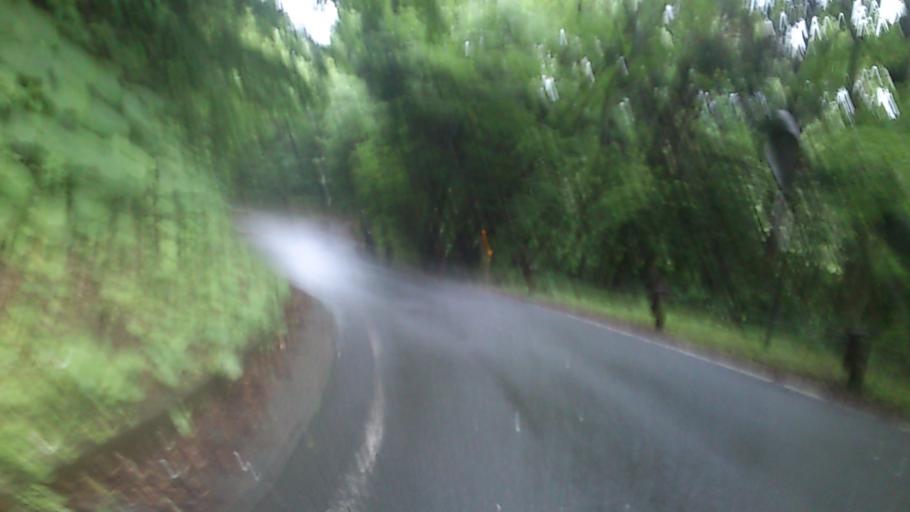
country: JP
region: Akita
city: Noshiromachi
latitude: 40.5609
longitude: 139.9627
